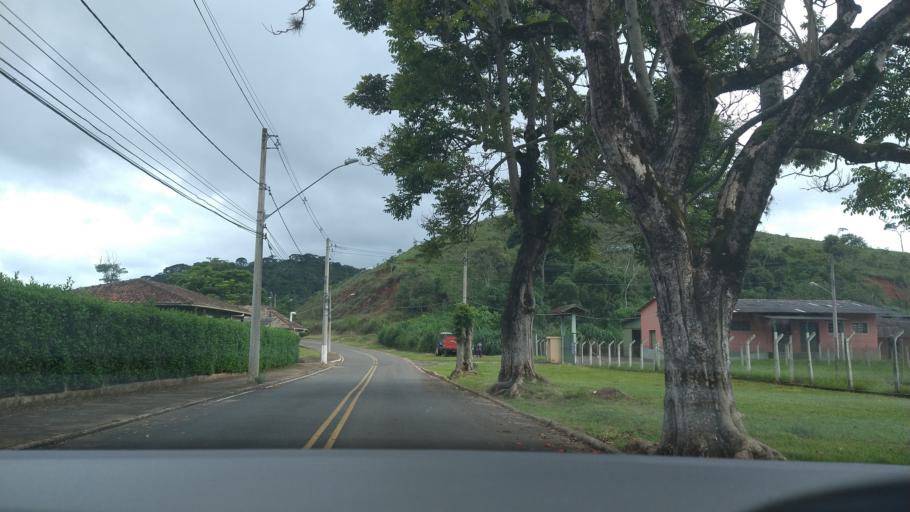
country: BR
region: Minas Gerais
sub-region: Vicosa
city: Vicosa
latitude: -20.7711
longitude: -42.8613
